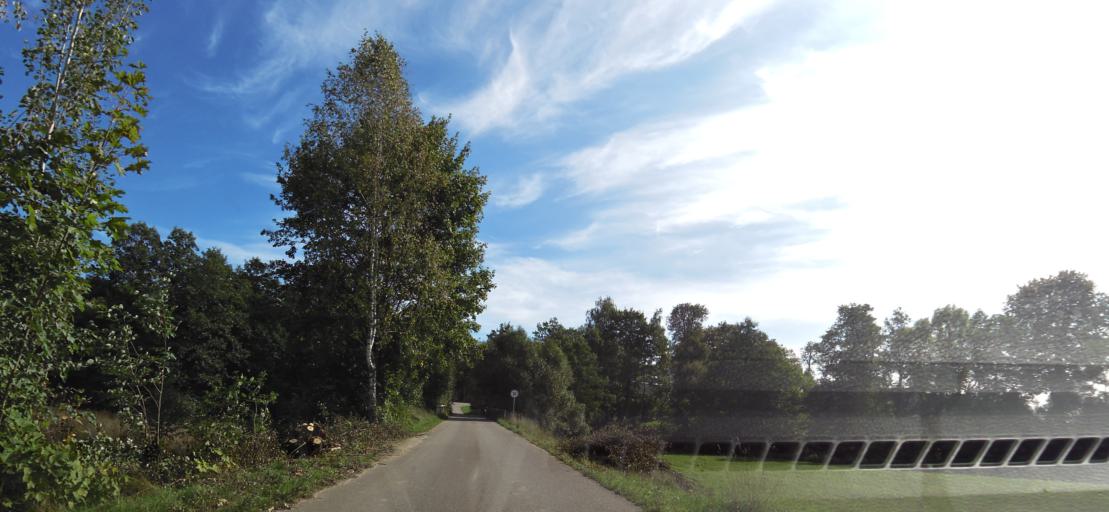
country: LT
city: Salcininkai
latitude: 54.4484
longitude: 25.5175
